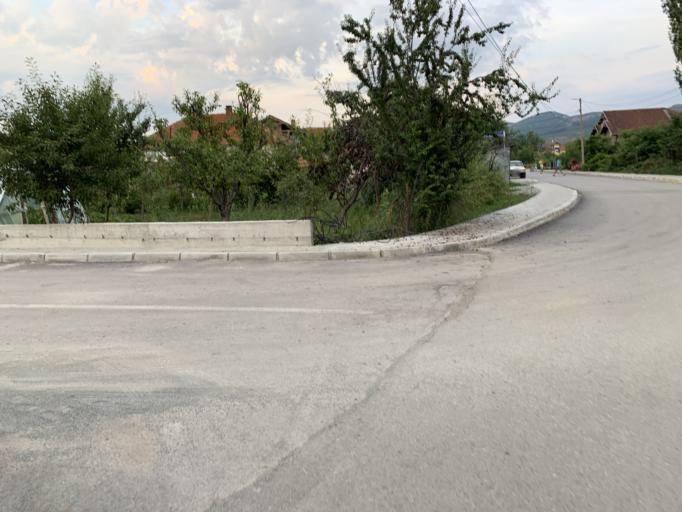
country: XK
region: Pristina
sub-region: Komuna e Prishtines
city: Pristina
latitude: 42.6003
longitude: 21.1882
